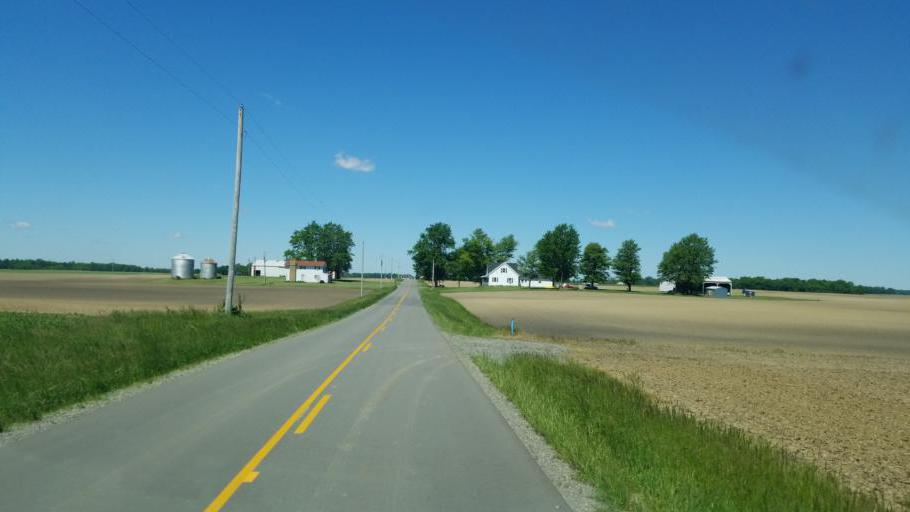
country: US
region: Ohio
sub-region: Logan County
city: Lakeview
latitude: 40.4173
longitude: -83.9551
